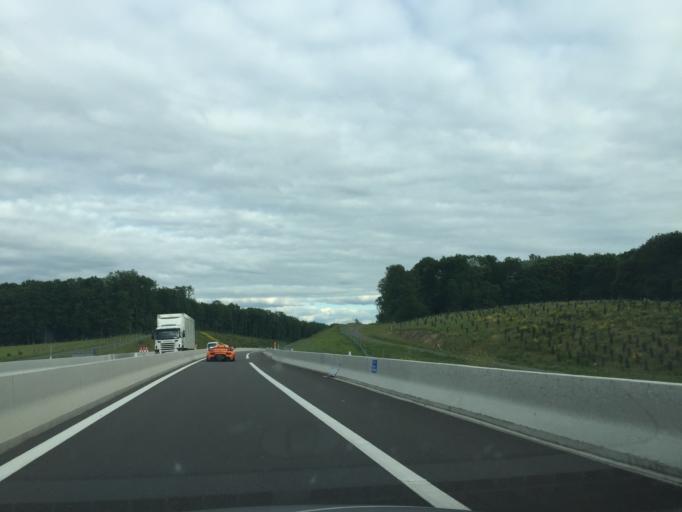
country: FR
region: Auvergne
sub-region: Departement de l'Allier
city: Vendat
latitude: 46.1371
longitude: 3.3553
